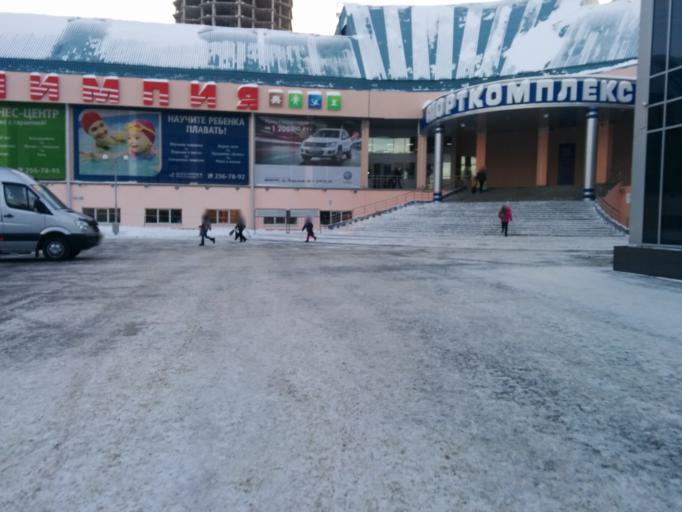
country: RU
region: Perm
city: Perm
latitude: 57.9771
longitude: 56.1870
